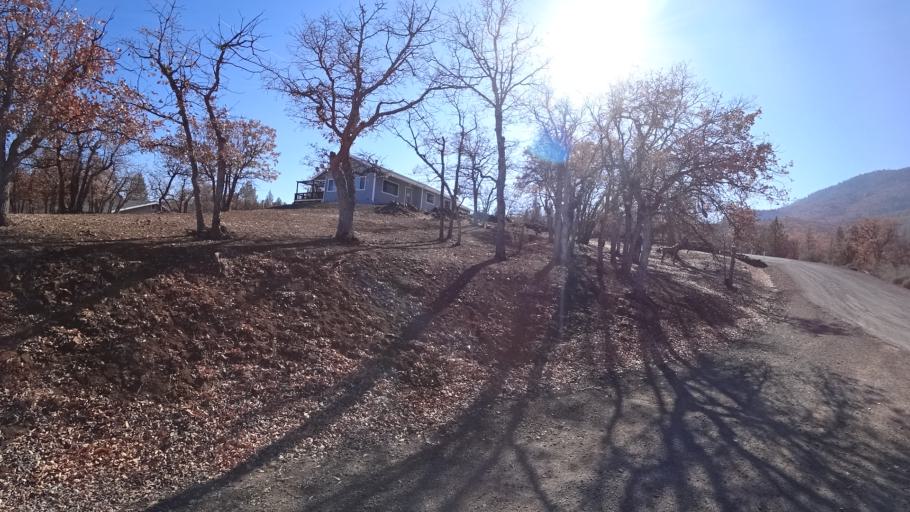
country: US
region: California
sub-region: Siskiyou County
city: Montague
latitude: 41.8855
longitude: -122.4910
